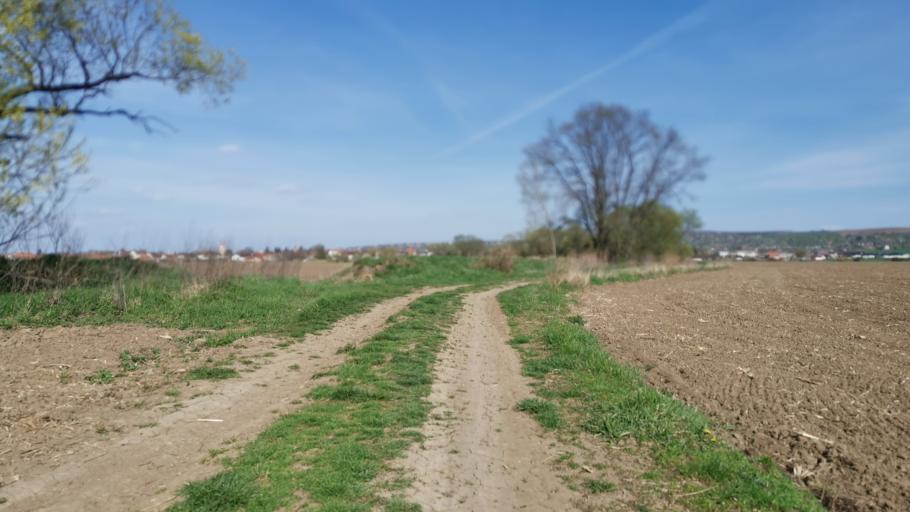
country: SK
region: Trnavsky
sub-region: Okres Skalica
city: Holic
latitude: 48.8207
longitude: 17.1817
